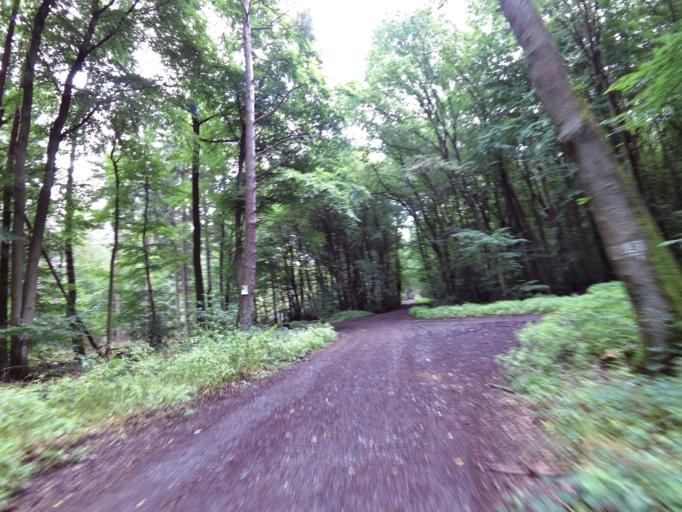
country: DE
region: Rheinland-Pfalz
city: Dernau
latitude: 50.5561
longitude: 7.0641
